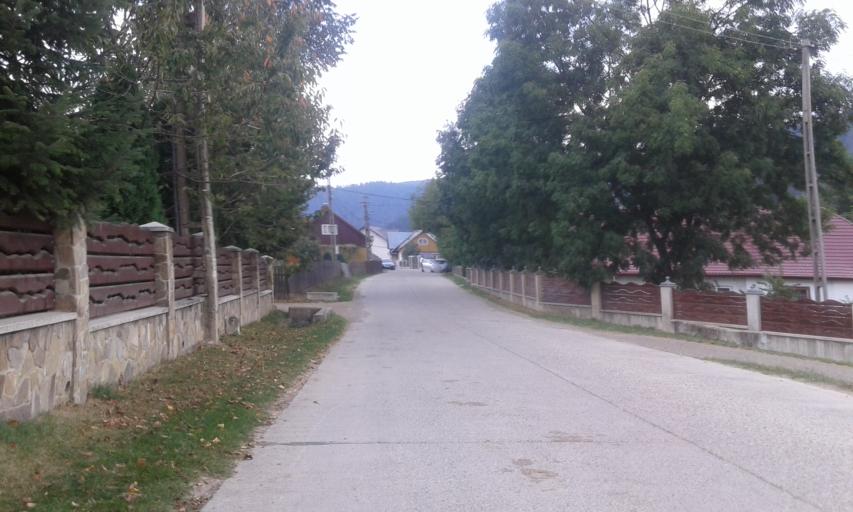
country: RO
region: Suceava
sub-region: Comuna Putna
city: Putna
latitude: 47.8674
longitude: 25.6097
